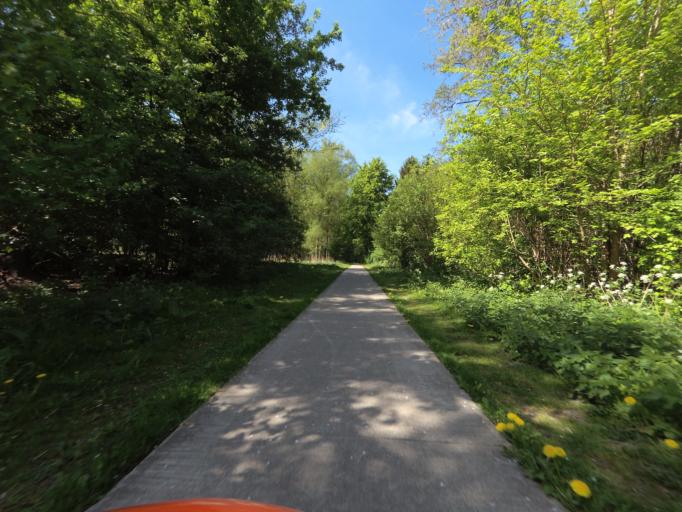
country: NL
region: Flevoland
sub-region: Gemeente Dronten
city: Dronten
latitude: 52.5249
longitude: 5.6917
